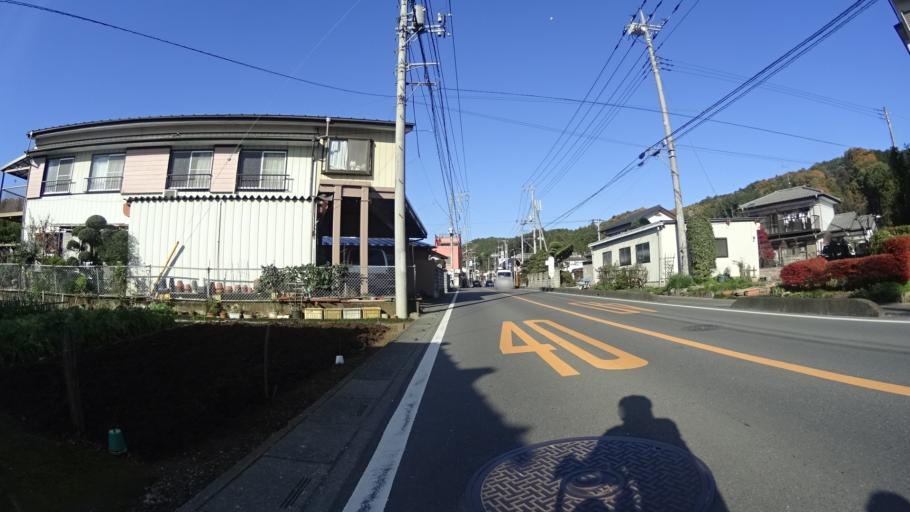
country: JP
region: Saitama
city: Hanno
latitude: 35.8584
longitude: 139.3006
